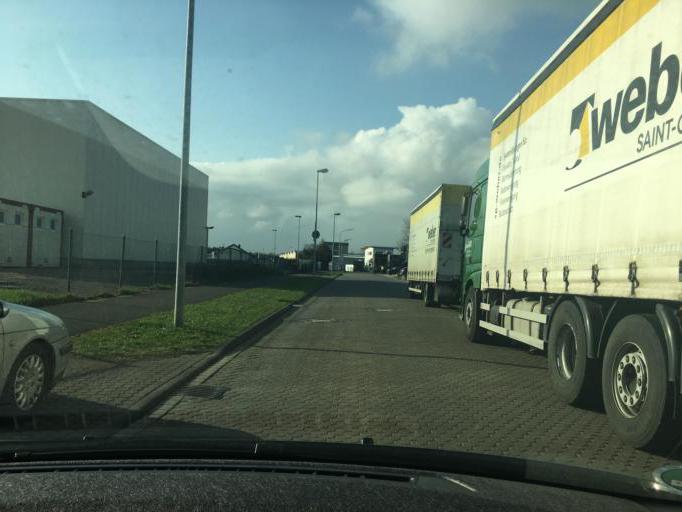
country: DE
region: North Rhine-Westphalia
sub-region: Regierungsbezirk Koln
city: Weilerswist
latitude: 50.7505
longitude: 6.8554
